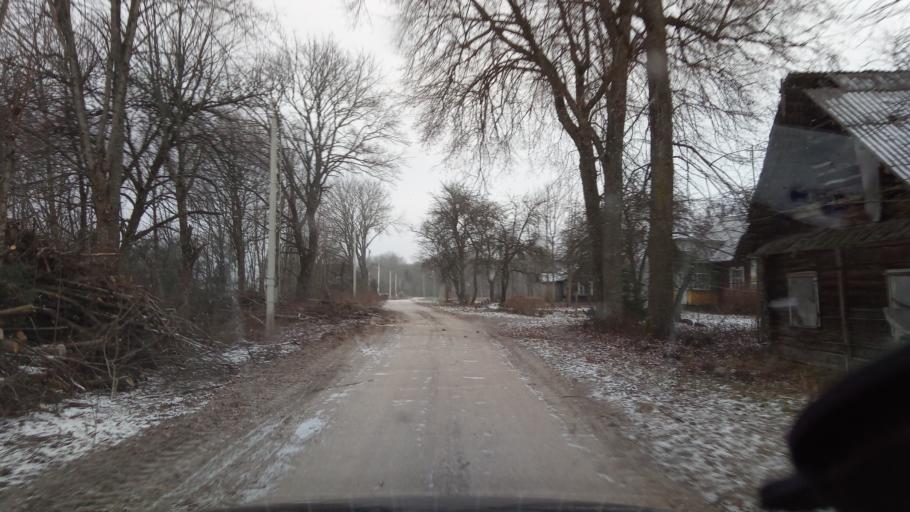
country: LT
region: Alytaus apskritis
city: Varena
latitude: 54.1283
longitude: 24.7044
